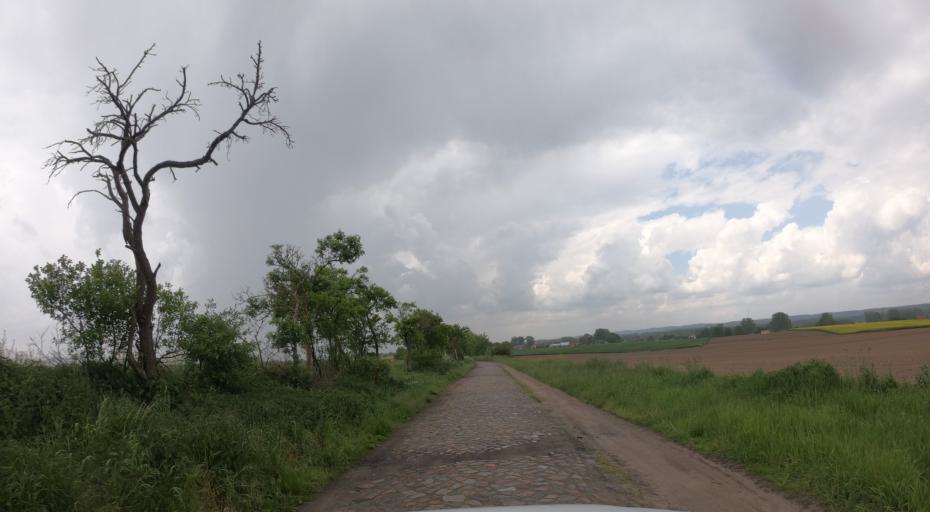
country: PL
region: West Pomeranian Voivodeship
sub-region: Powiat pyrzycki
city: Bielice
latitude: 53.2656
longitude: 14.6935
